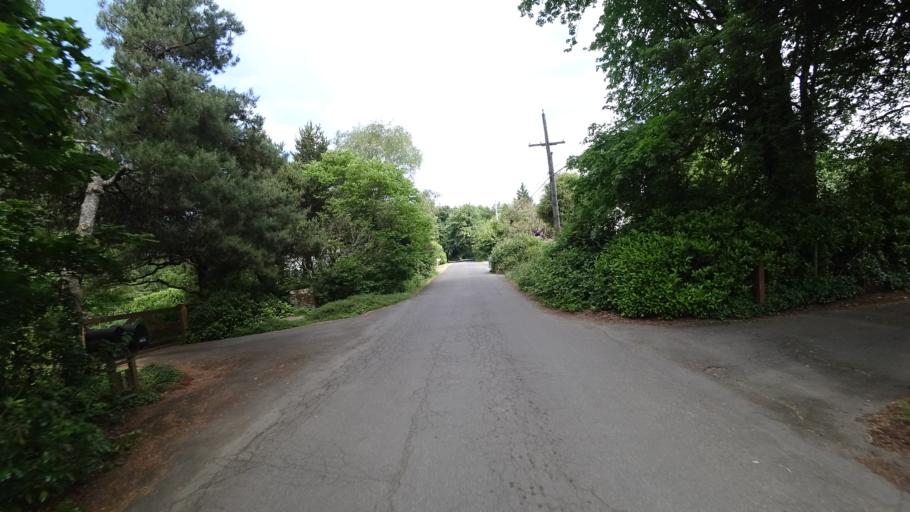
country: US
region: Oregon
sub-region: Clackamas County
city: Lake Oswego
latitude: 45.4494
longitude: -122.6834
